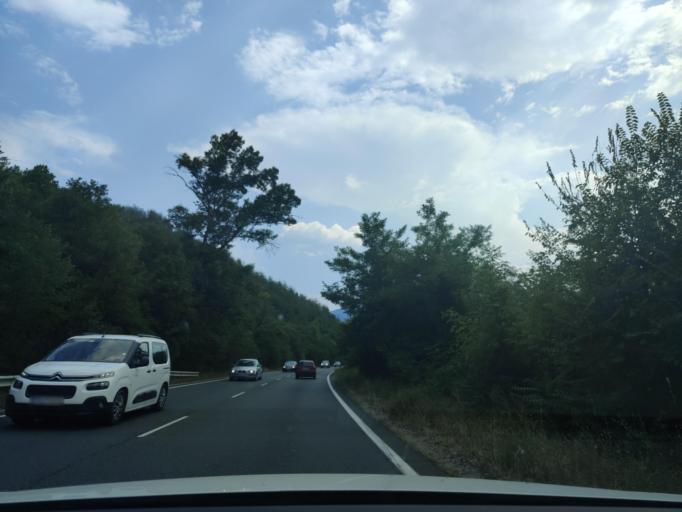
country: BG
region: Blagoevgrad
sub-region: Obshtina Simitli
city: Simitli
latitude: 41.8806
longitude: 23.1204
